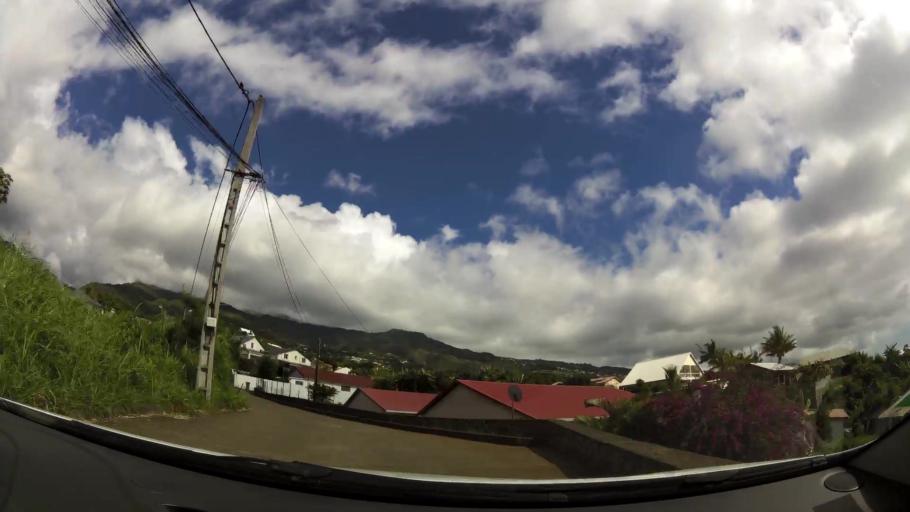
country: RE
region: Reunion
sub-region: Reunion
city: Sainte-Marie
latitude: -20.9267
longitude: 55.5002
